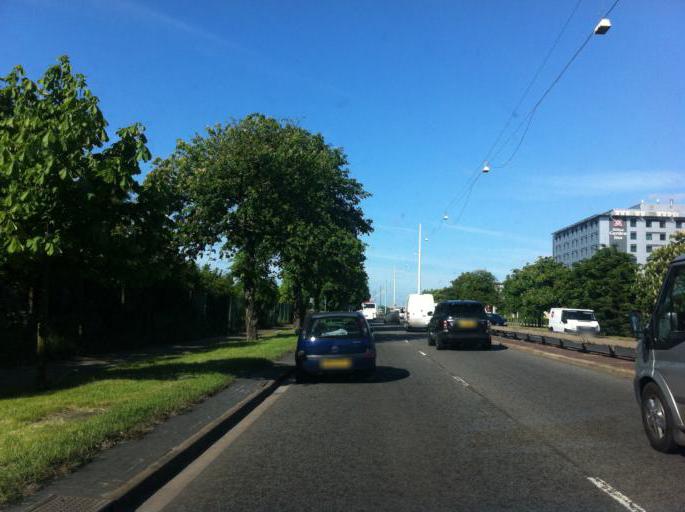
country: GB
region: England
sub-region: Greater London
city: Feltham
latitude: 51.4687
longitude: -0.4148
